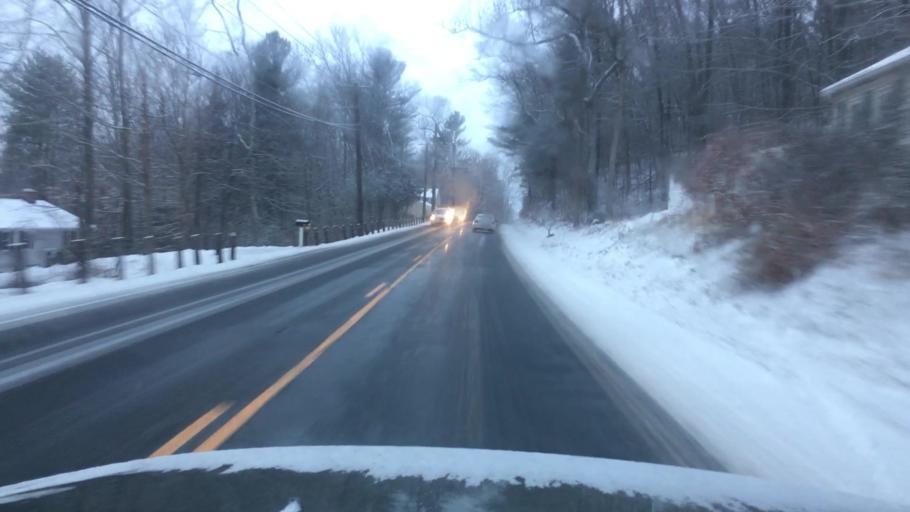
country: US
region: Connecticut
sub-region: Tolland County
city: Somers
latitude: 41.9829
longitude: -72.4179
